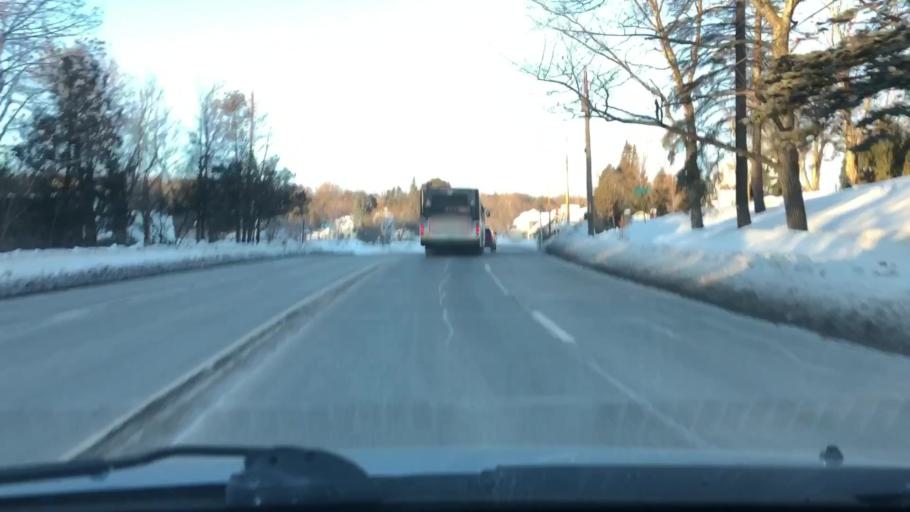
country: US
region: Minnesota
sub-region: Saint Louis County
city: Arnold
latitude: 46.8360
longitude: -92.0748
